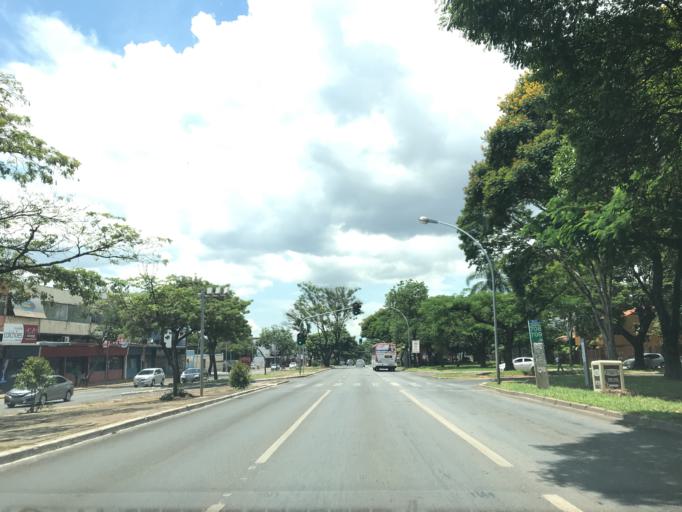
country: BR
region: Federal District
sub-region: Brasilia
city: Brasilia
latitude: -15.8128
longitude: -47.9069
